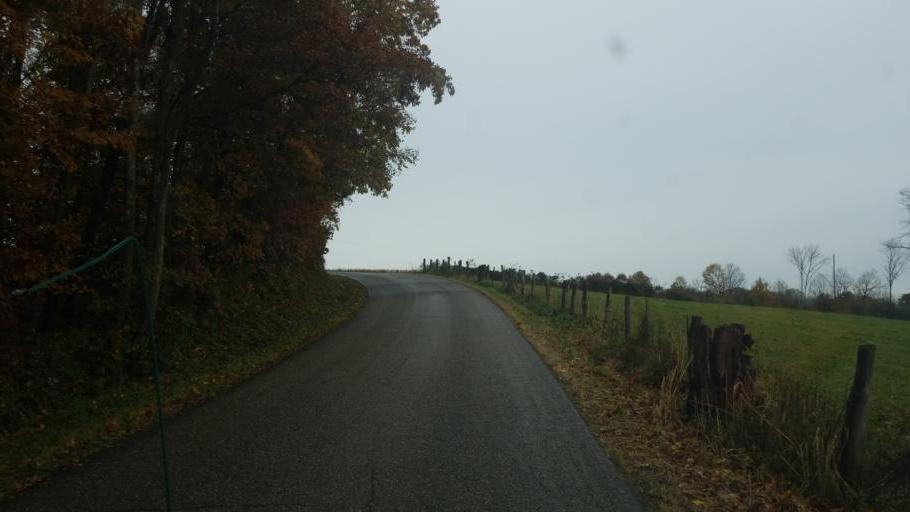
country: US
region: Ohio
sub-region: Washington County
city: Beverly
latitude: 39.5438
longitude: -81.7046
